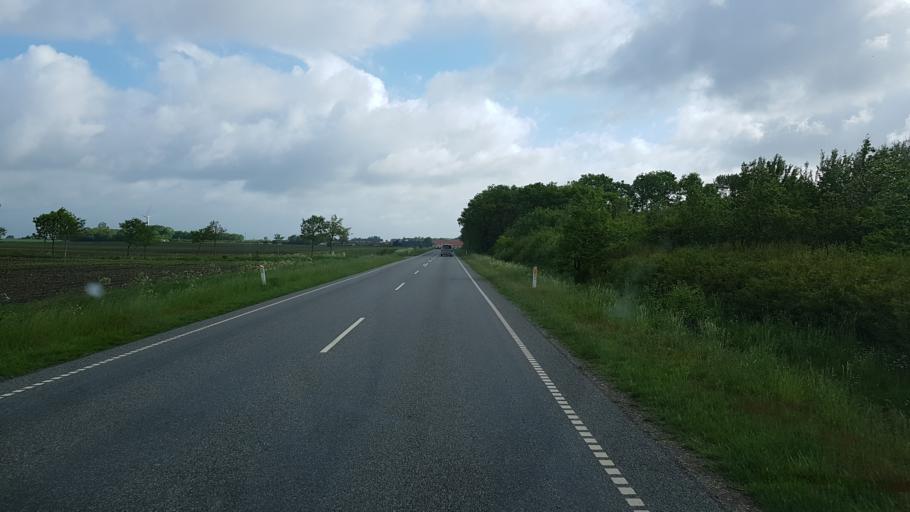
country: DK
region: South Denmark
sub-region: Vejen Kommune
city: Vejen
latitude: 55.4162
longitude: 9.1369
